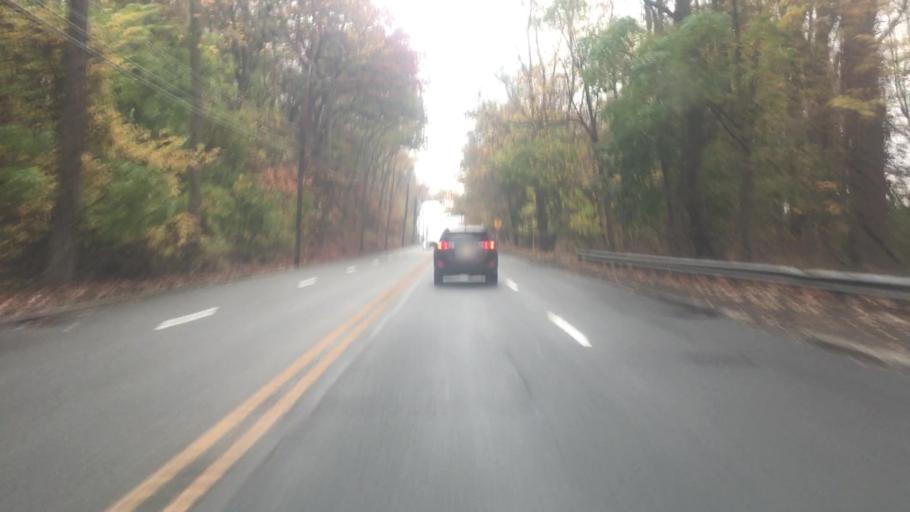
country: US
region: New Jersey
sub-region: Bergen County
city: Oakland
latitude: 40.9744
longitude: -74.2671
